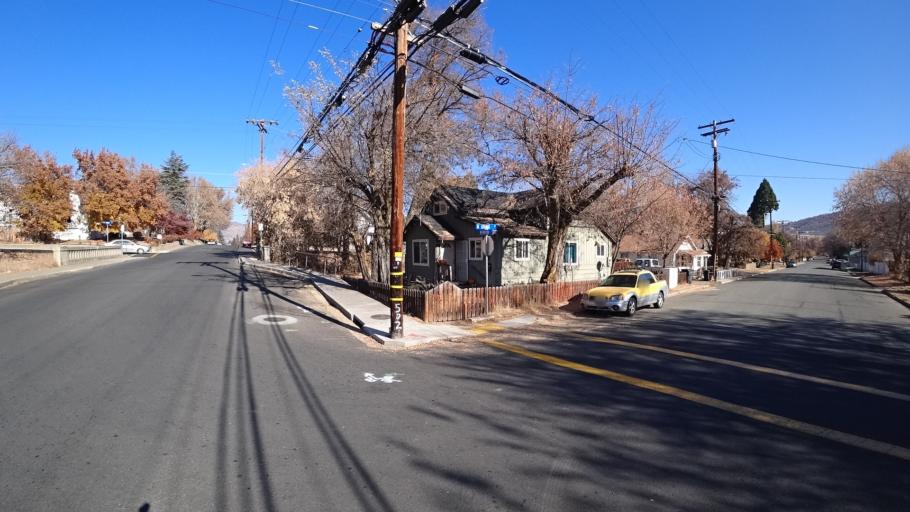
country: US
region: California
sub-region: Siskiyou County
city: Yreka
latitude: 41.7362
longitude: -122.6368
